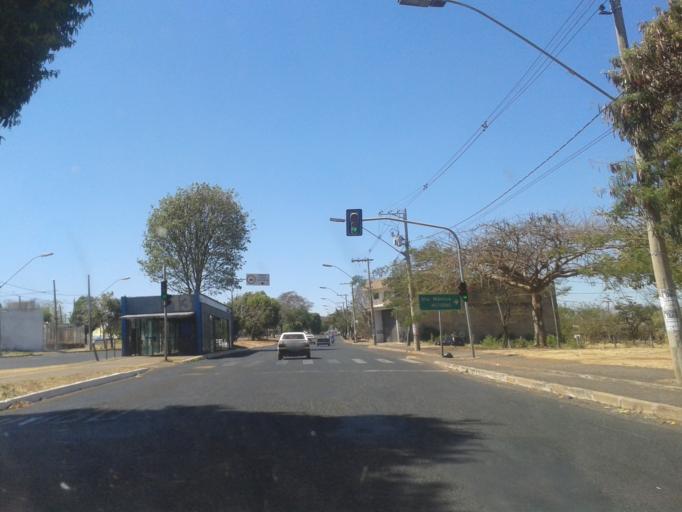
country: BR
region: Minas Gerais
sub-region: Uberlandia
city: Uberlandia
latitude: -18.9331
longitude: -48.2352
